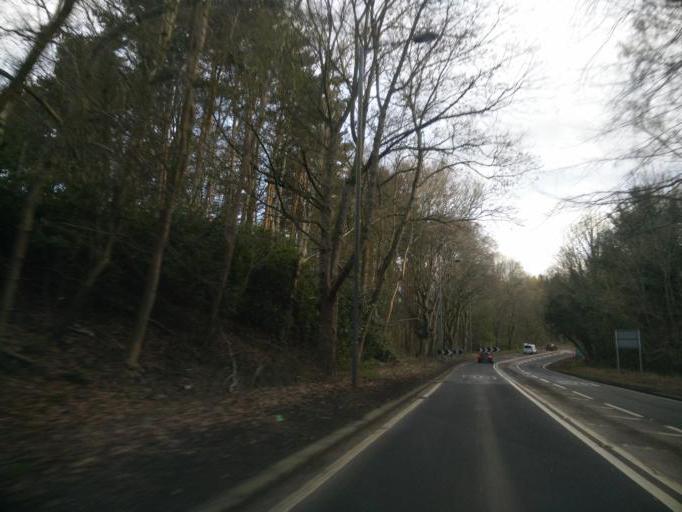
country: GB
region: England
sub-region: County Durham
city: Ushaw Moor
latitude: 54.7335
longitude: -1.6584
